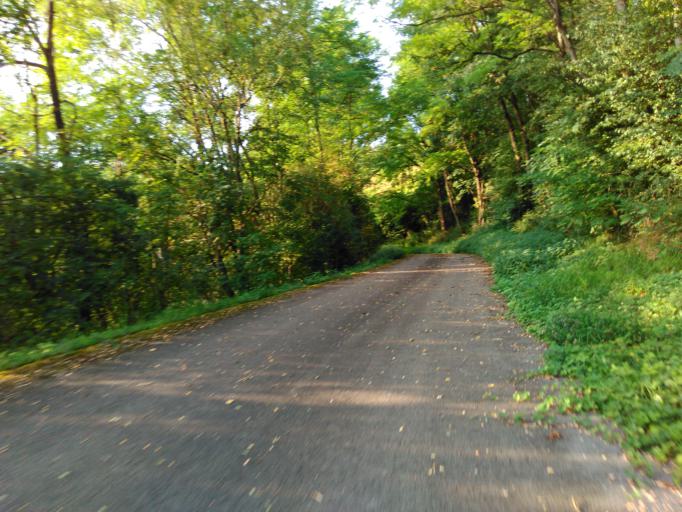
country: LU
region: Grevenmacher
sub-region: Canton de Remich
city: Lenningen
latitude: 49.6125
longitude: 6.3727
